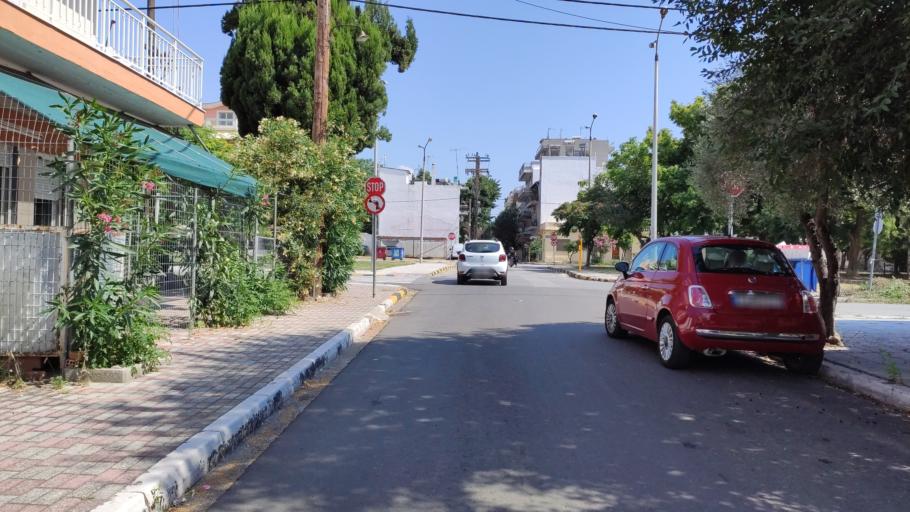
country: GR
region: East Macedonia and Thrace
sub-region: Nomos Rodopis
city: Komotini
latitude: 41.1154
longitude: 25.3917
